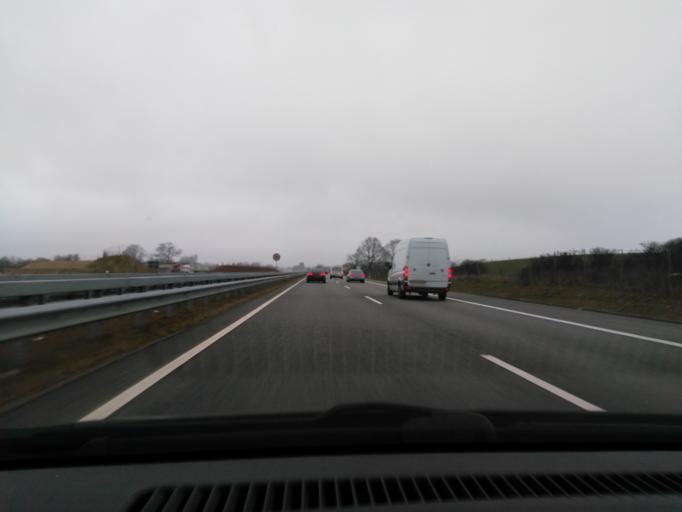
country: DE
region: Schleswig-Holstein
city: Stolpe
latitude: 54.1373
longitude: 10.2139
